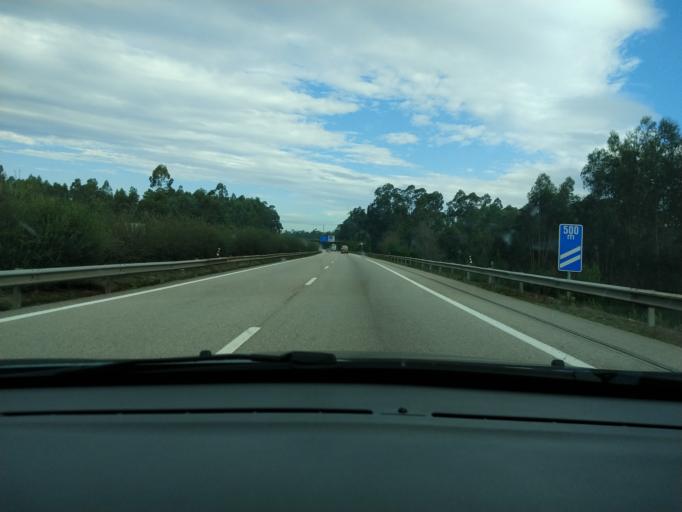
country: PT
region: Aveiro
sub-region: Estarreja
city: Beduido
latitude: 40.7730
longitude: -8.5434
